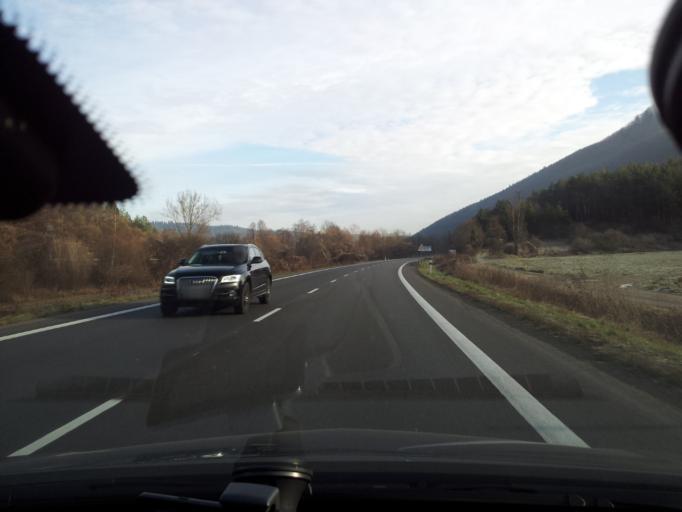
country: SK
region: Banskobystricky
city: Hrochot,Slovakia
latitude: 48.7735
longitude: 19.2987
